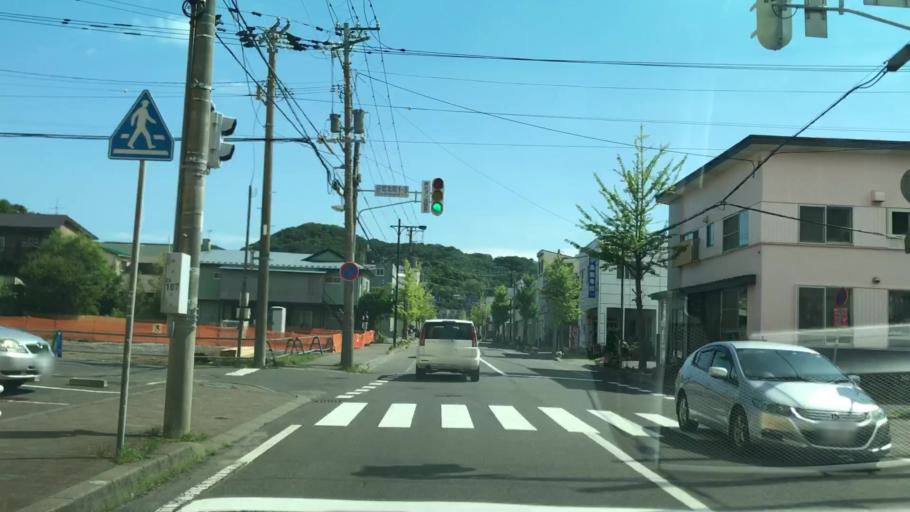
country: JP
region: Hokkaido
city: Muroran
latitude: 42.3161
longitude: 140.9898
